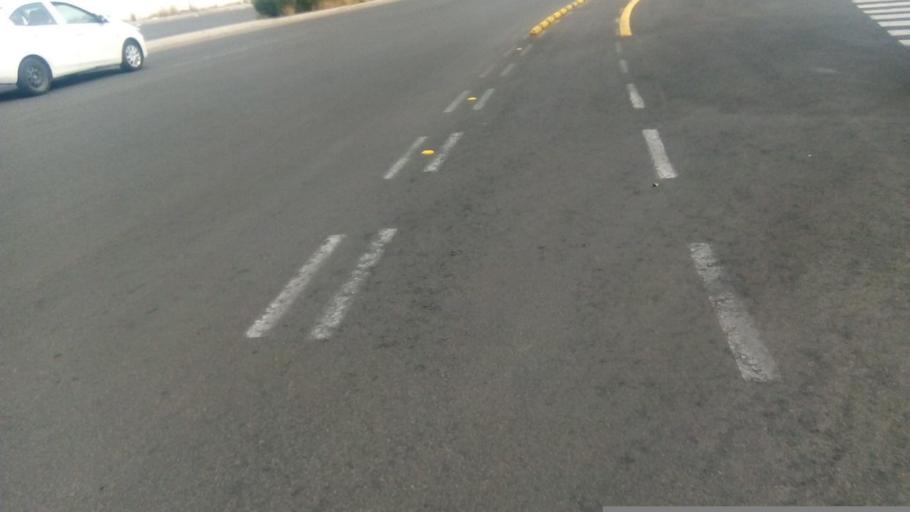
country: MX
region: Queretaro
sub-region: Queretaro
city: Santiago de Queretaro
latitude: 20.6159
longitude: -100.4029
